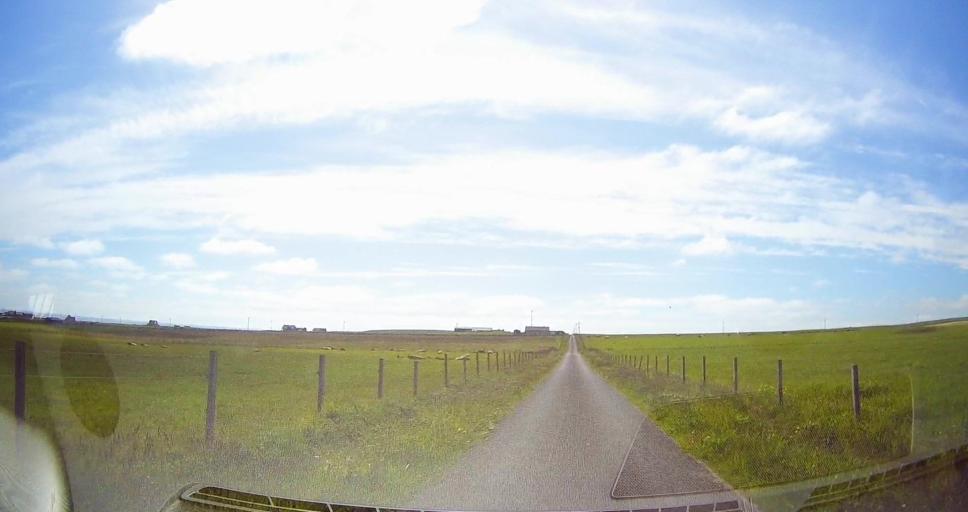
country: GB
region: Scotland
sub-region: Orkney Islands
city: Kirkwall
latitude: 58.8347
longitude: -2.9009
